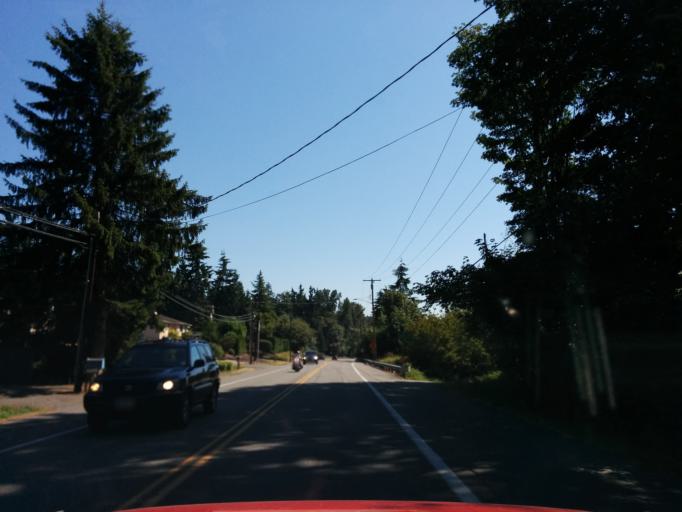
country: US
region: Washington
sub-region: King County
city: Sammamish
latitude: 47.6153
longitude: -122.0679
